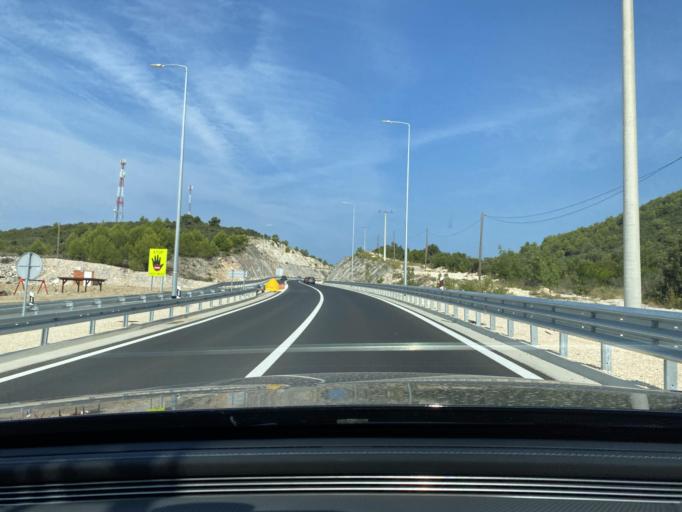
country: HR
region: Dubrovacko-Neretvanska
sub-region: Grad Dubrovnik
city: Opuzen
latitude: 42.9440
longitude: 17.5401
